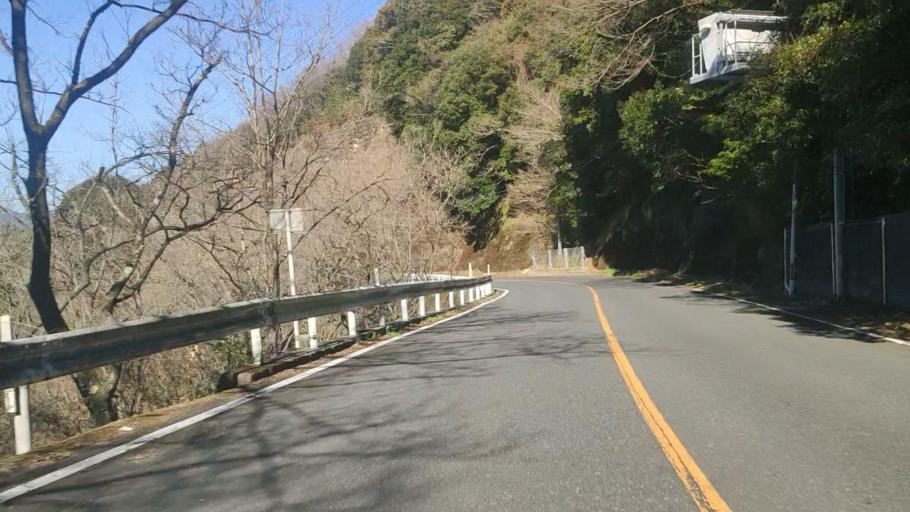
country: JP
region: Oita
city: Saiki
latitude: 32.8876
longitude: 131.9437
